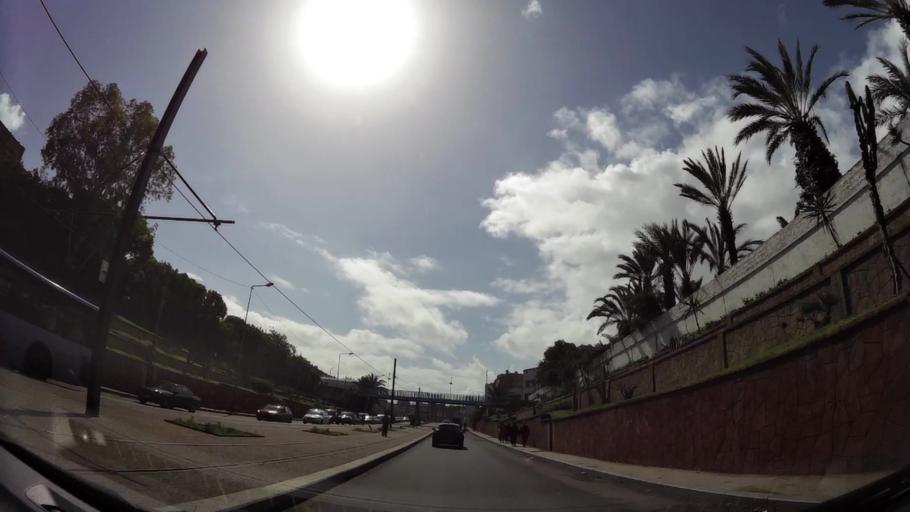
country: MA
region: Grand Casablanca
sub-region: Casablanca
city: Casablanca
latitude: 33.5677
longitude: -7.6105
